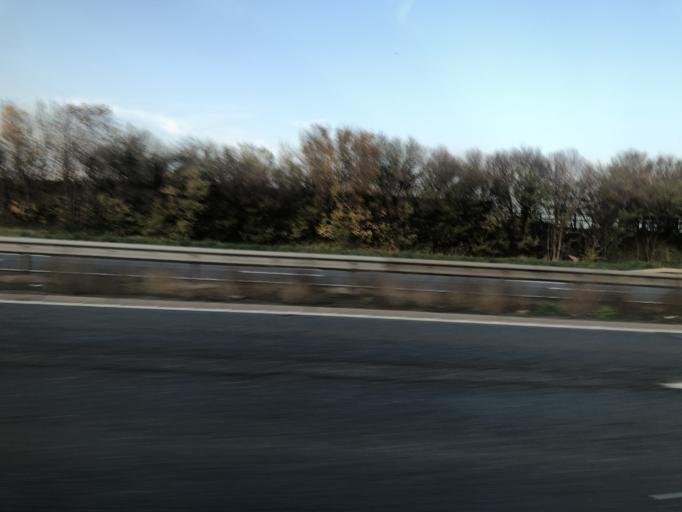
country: GB
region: England
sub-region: Kent
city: Dartford
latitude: 51.4269
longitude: 0.2174
